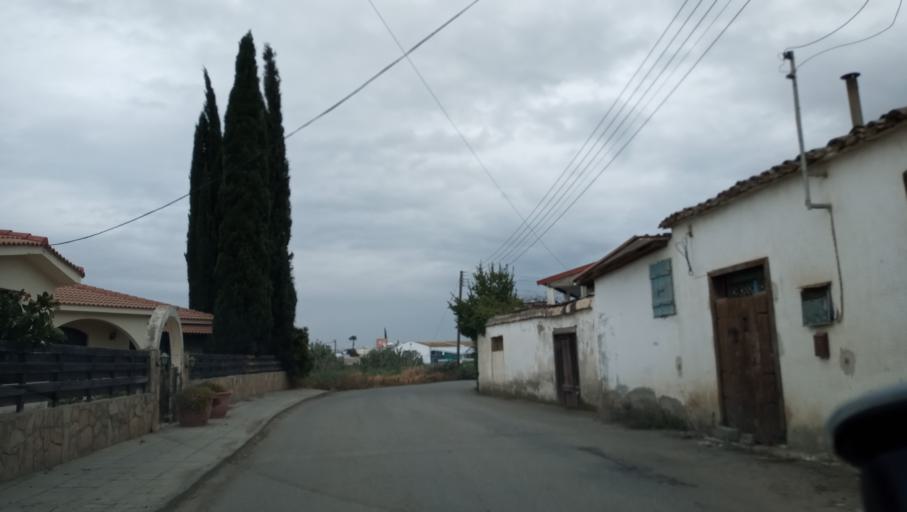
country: CY
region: Lefkosia
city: Kato Deftera
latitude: 35.0819
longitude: 33.2712
